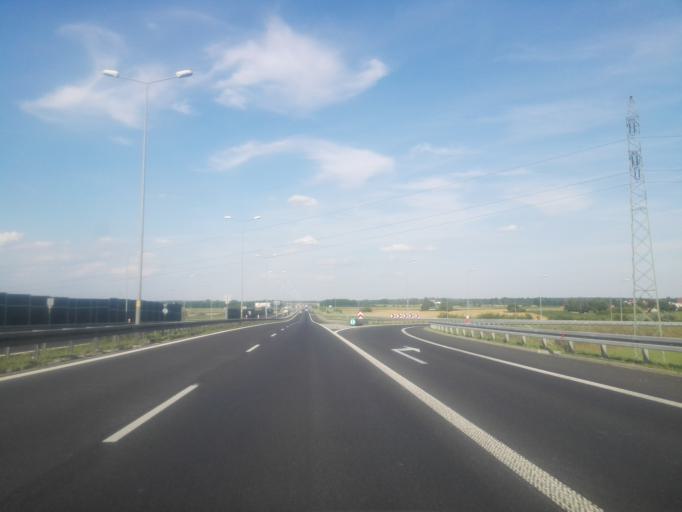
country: PL
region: Lower Silesian Voivodeship
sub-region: Powiat olesnicki
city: Olesnica
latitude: 51.2292
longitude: 17.3702
